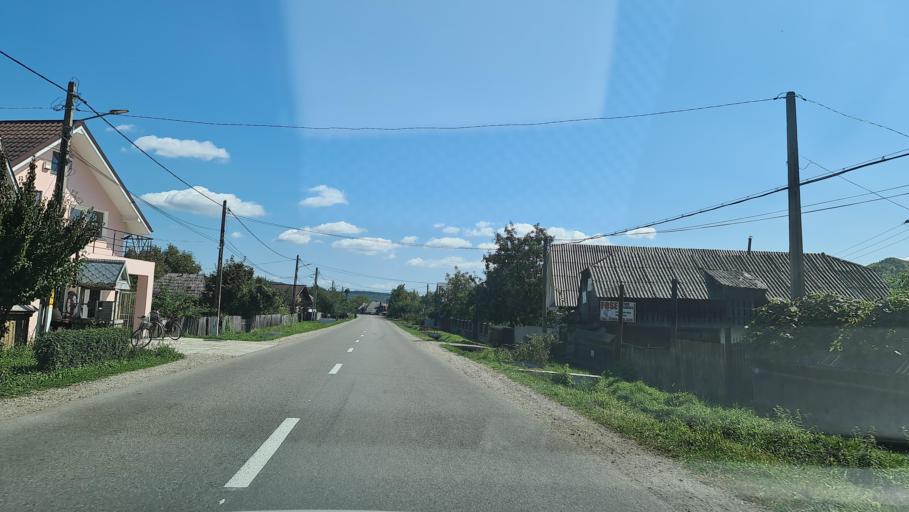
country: RO
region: Bacau
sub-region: Comuna Balcani
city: Frumoasa
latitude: 46.6653
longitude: 26.5299
